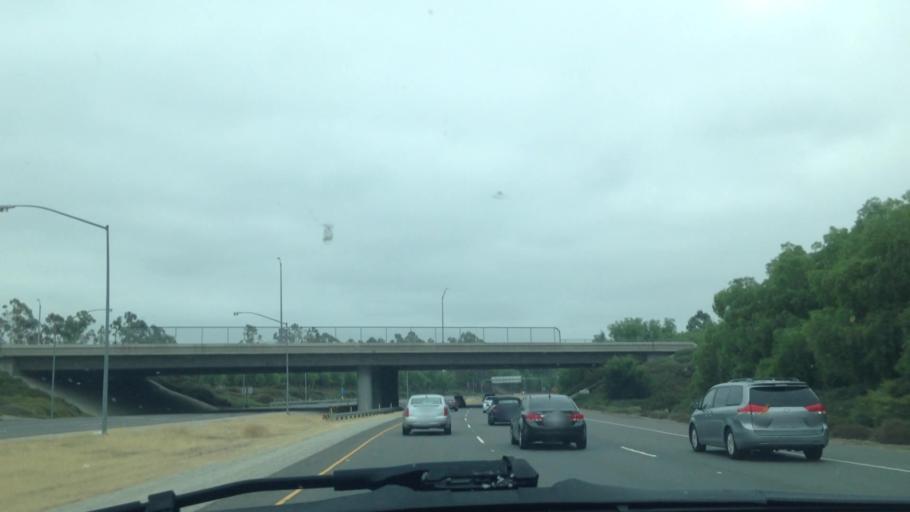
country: US
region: California
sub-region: Orange County
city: North Tustin
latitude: 33.7276
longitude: -117.7781
